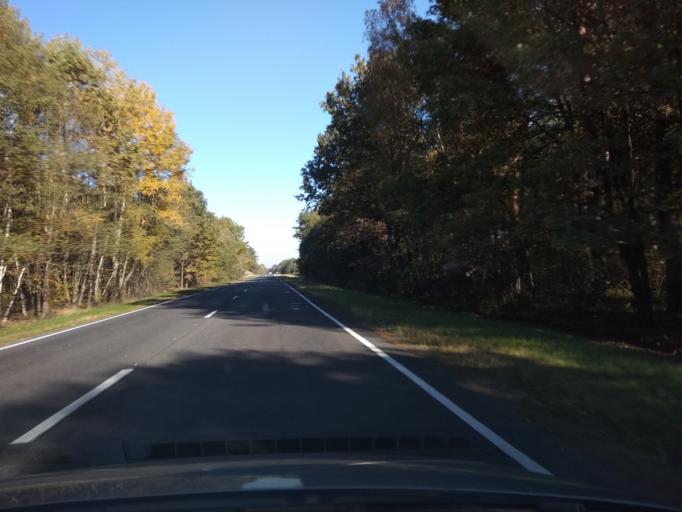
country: BY
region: Brest
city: Kobryn
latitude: 52.0482
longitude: 24.2767
